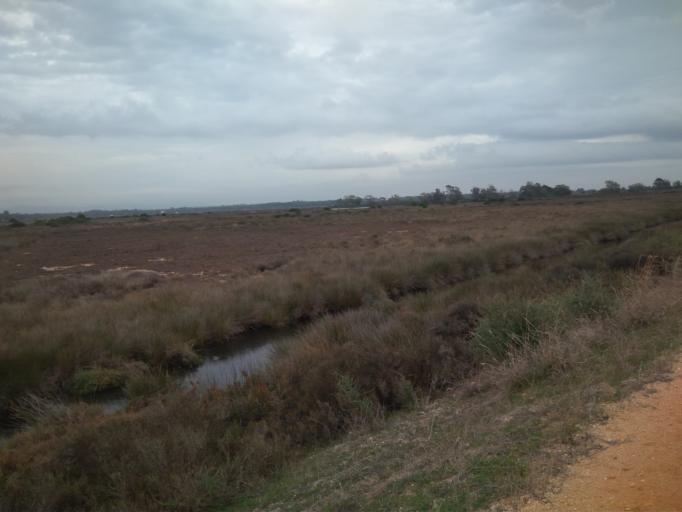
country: PT
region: Faro
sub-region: Loule
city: Almancil
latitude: 37.0217
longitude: -8.0080
